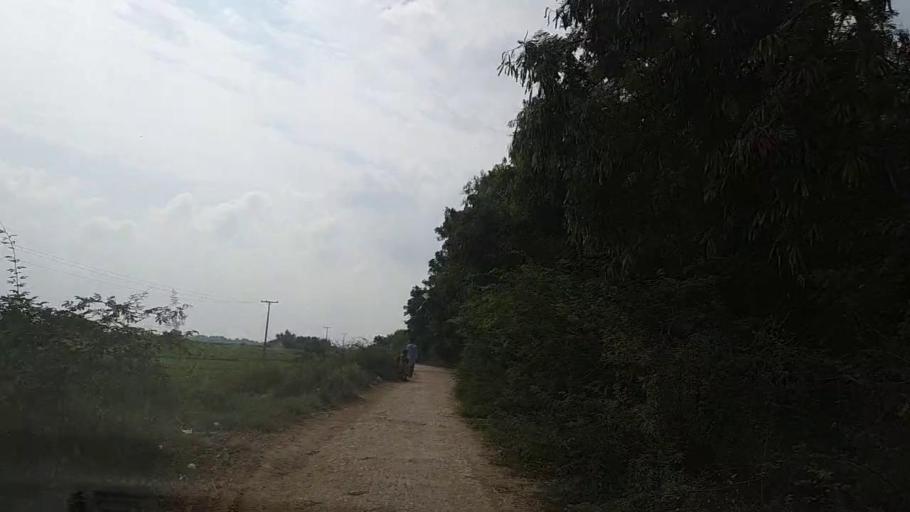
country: PK
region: Sindh
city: Mirpur Batoro
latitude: 24.5934
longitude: 68.1287
